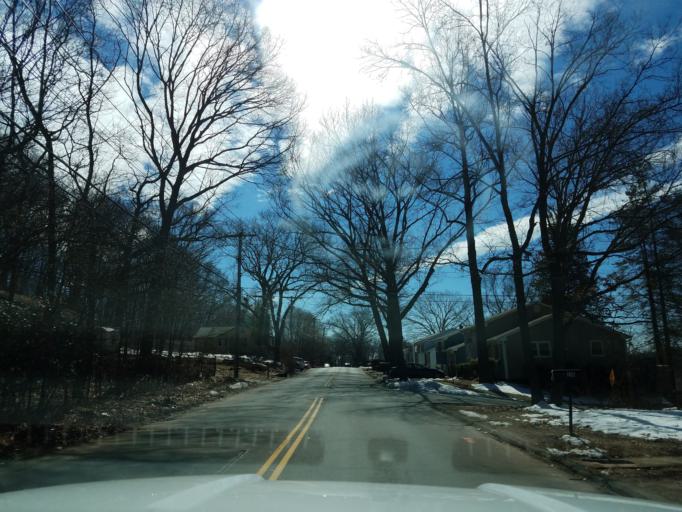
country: US
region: Connecticut
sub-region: New Haven County
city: West Haven
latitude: 41.2948
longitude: -72.9750
